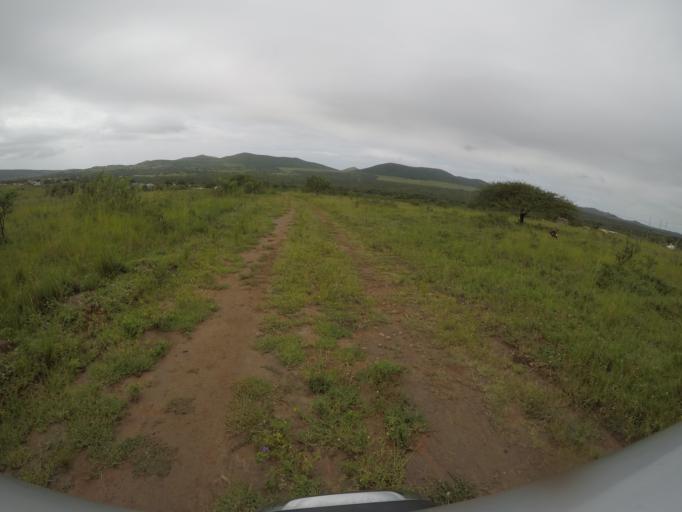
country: ZA
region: KwaZulu-Natal
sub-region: uThungulu District Municipality
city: Empangeni
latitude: -28.6147
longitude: 31.8411
